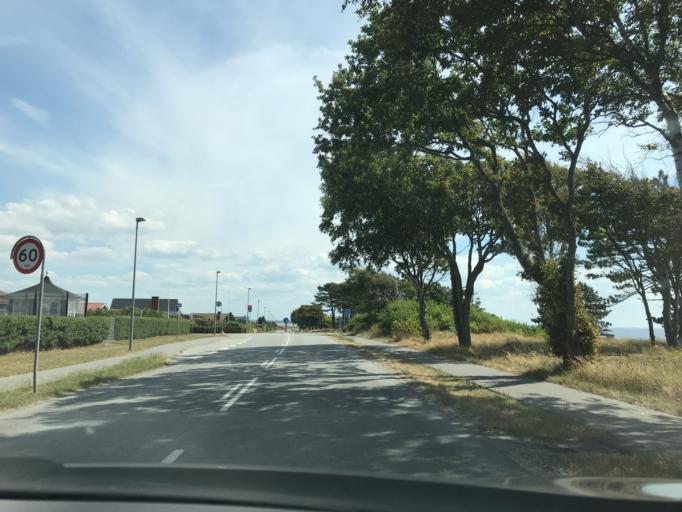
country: DK
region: Central Jutland
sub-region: Ringkobing-Skjern Kommune
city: Ringkobing
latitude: 56.0725
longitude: 8.2729
